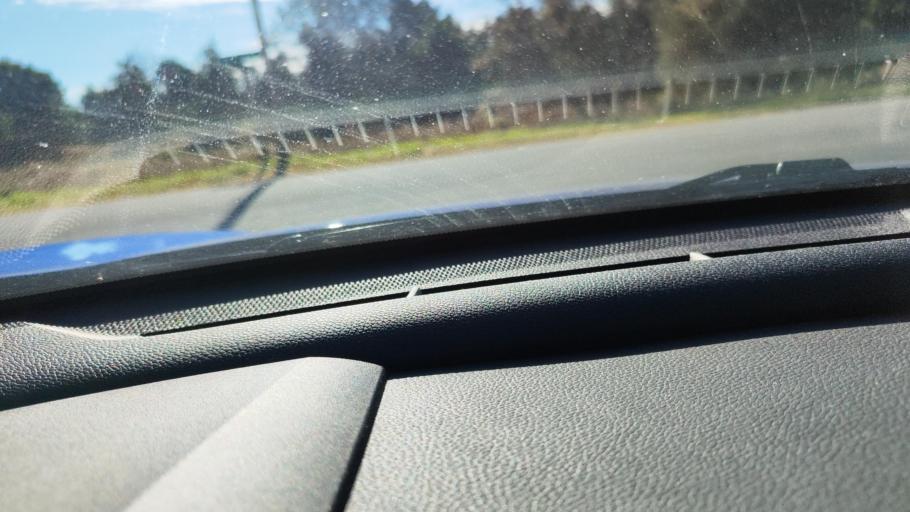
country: CA
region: Ontario
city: Angus
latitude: 44.3569
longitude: -79.9786
